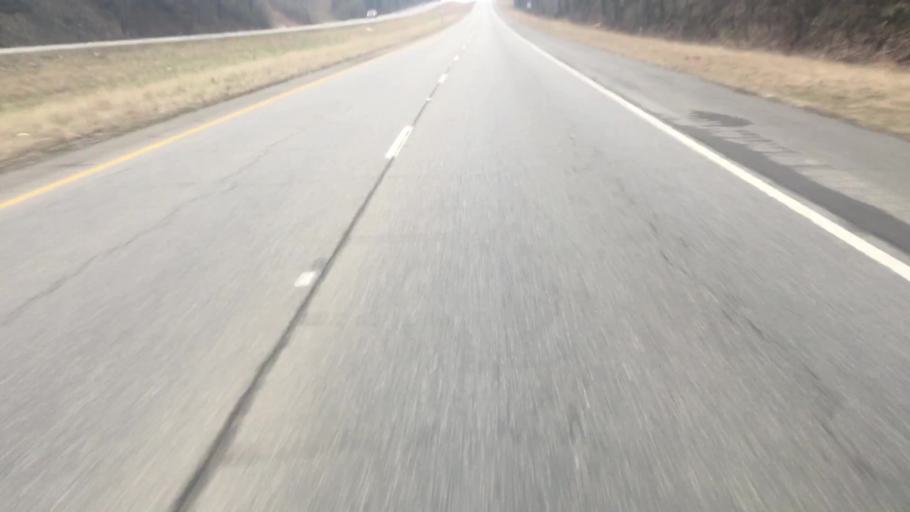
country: US
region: Alabama
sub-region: Walker County
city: Sumiton
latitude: 33.7710
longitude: -87.0725
